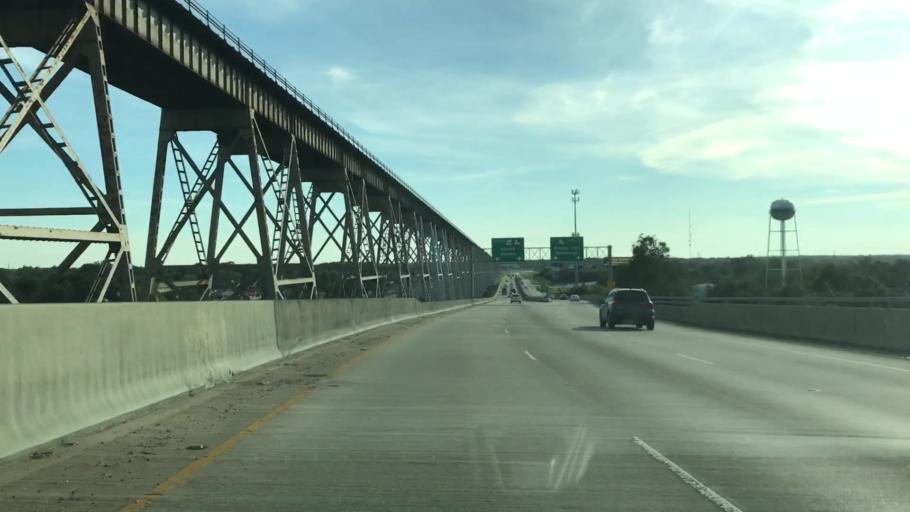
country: US
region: Louisiana
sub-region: Jefferson Parish
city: Bridge City
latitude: 29.9357
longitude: -90.1634
